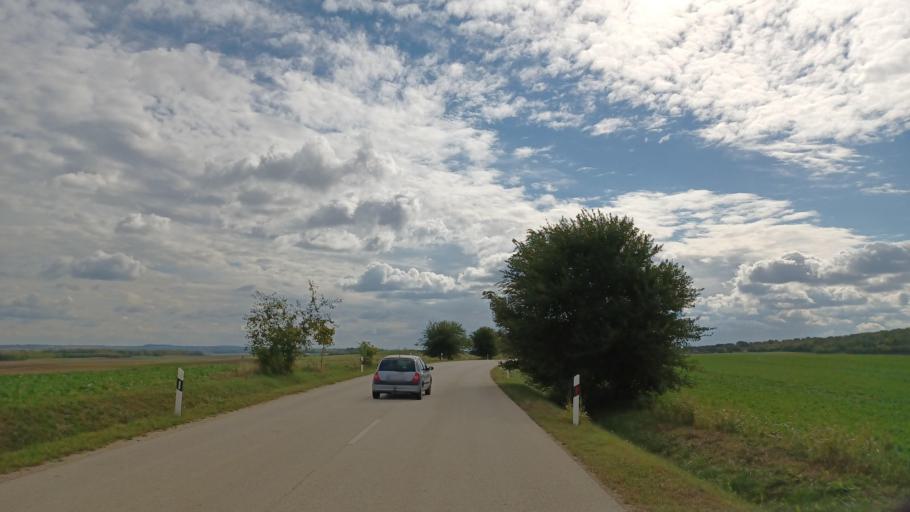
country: HU
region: Tolna
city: Simontornya
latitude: 46.7212
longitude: 18.5773
